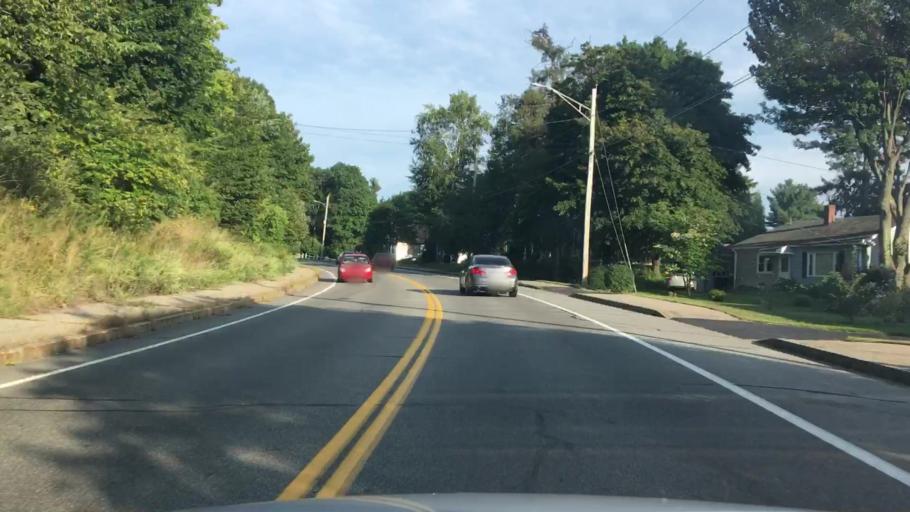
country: US
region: Maine
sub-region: Cumberland County
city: South Portland Gardens
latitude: 43.6627
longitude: -70.3030
